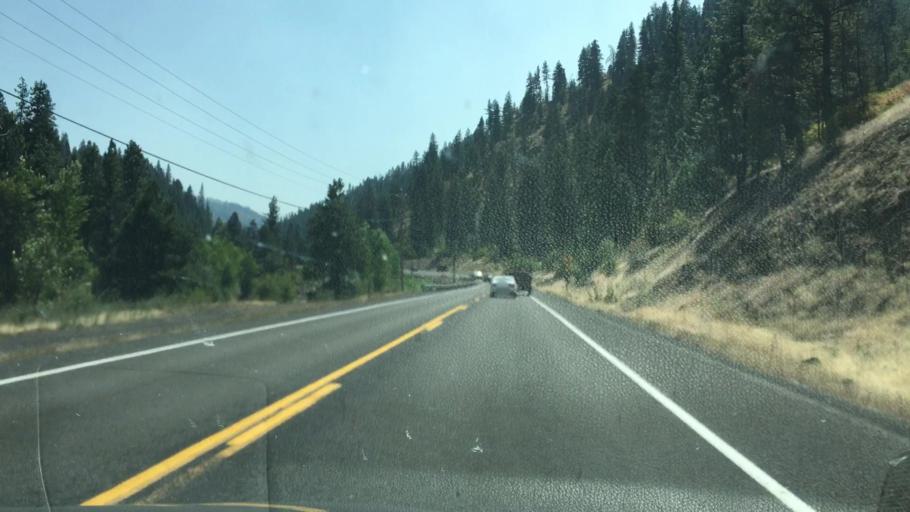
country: US
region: Idaho
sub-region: Valley County
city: McCall
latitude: 45.2079
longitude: -116.3131
